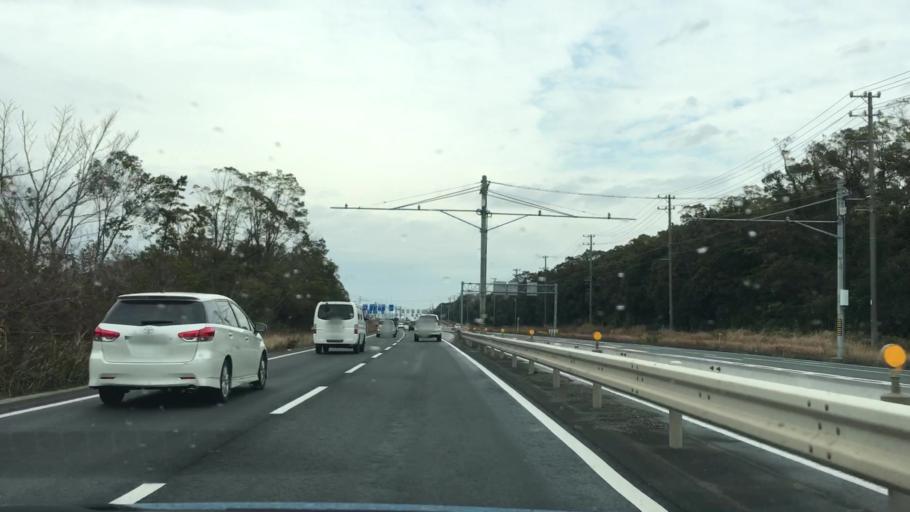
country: JP
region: Aichi
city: Toyohashi
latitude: 34.7149
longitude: 137.3384
